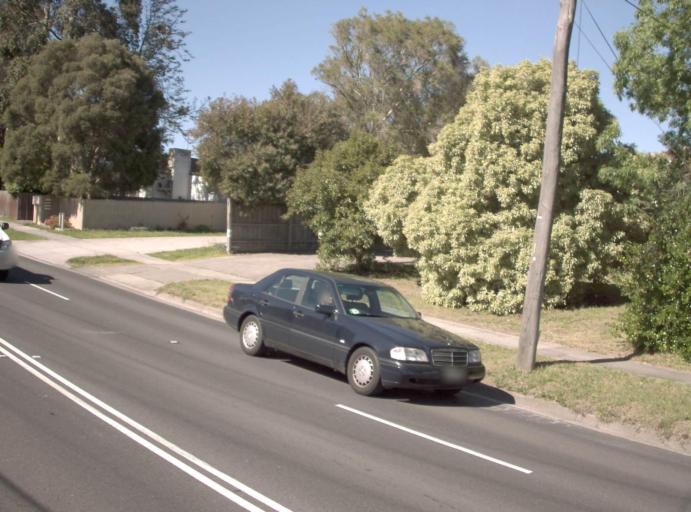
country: AU
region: Victoria
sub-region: Knox
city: Bayswater
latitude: -37.8667
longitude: 145.2626
